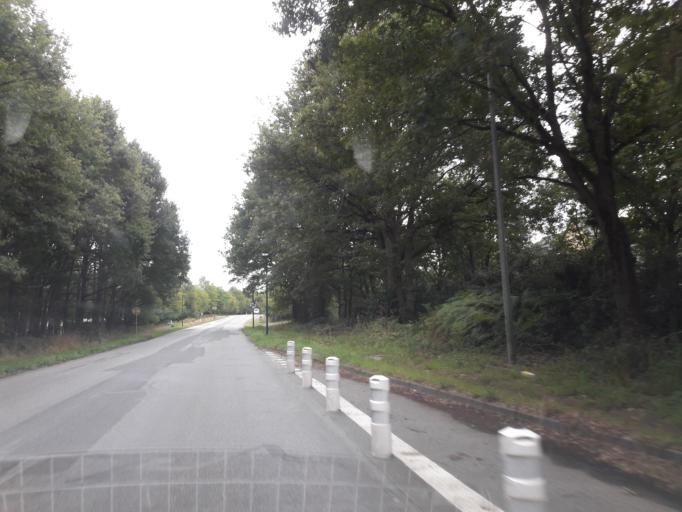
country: FR
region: Brittany
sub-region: Departement d'Ille-et-Vilaine
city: Orgeres
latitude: 48.0055
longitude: -1.6981
